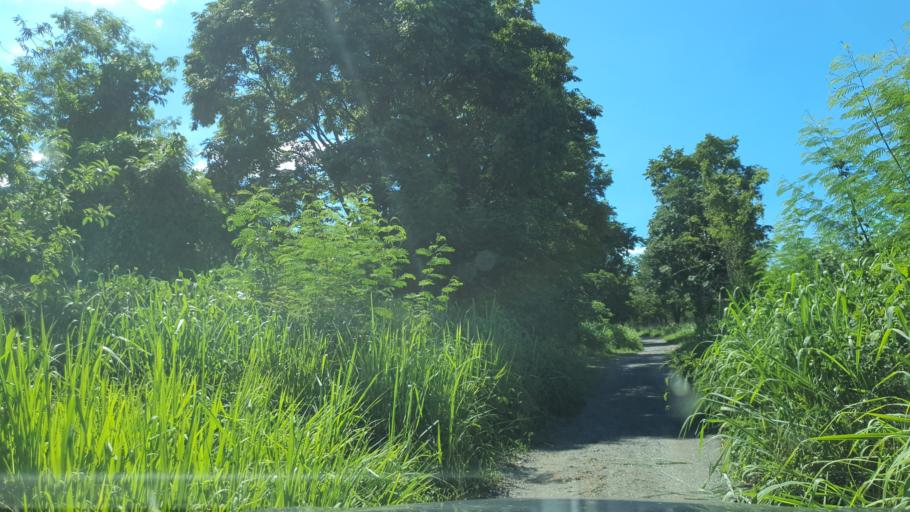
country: TH
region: Chiang Mai
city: Mae On
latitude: 18.7648
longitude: 99.2425
